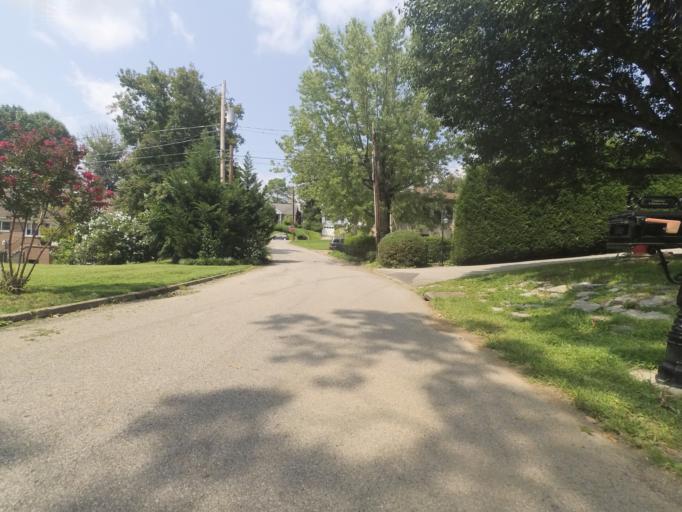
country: US
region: West Virginia
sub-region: Cabell County
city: Huntington
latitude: 38.4053
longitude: -82.4194
